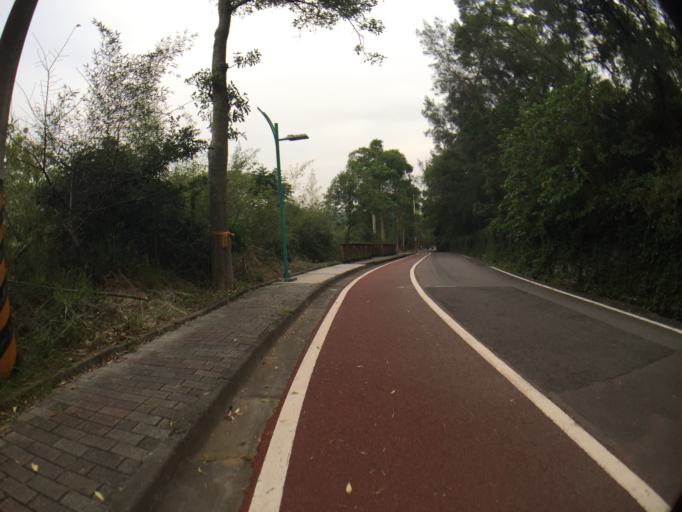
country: TW
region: Taiwan
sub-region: Hsinchu
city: Hsinchu
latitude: 24.7732
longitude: 120.9726
